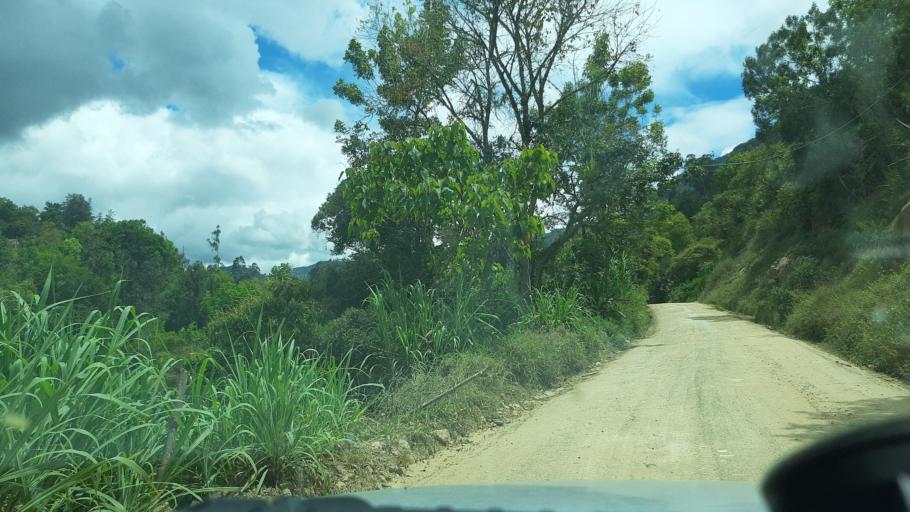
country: CO
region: Cundinamarca
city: Umbita
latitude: 5.2204
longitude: -73.4266
